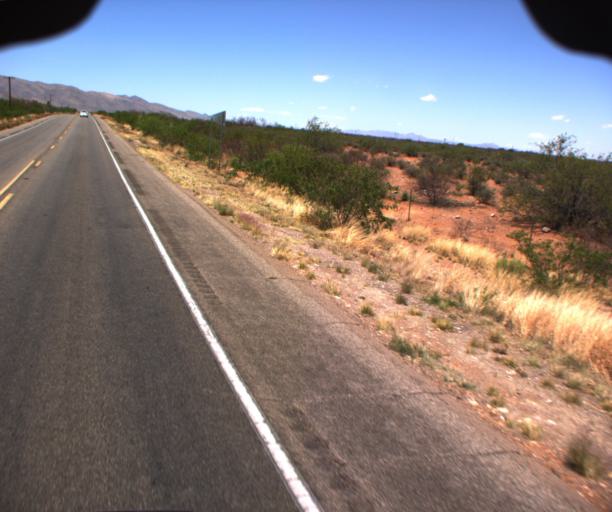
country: US
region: Arizona
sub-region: Cochise County
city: Bisbee
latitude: 31.3871
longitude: -109.7600
